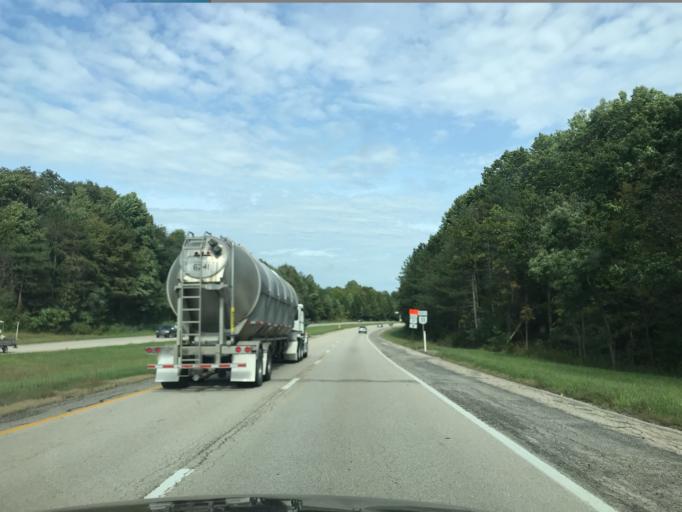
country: US
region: Ohio
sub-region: Ashtabula County
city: Edgewood
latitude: 41.8477
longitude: -80.7670
